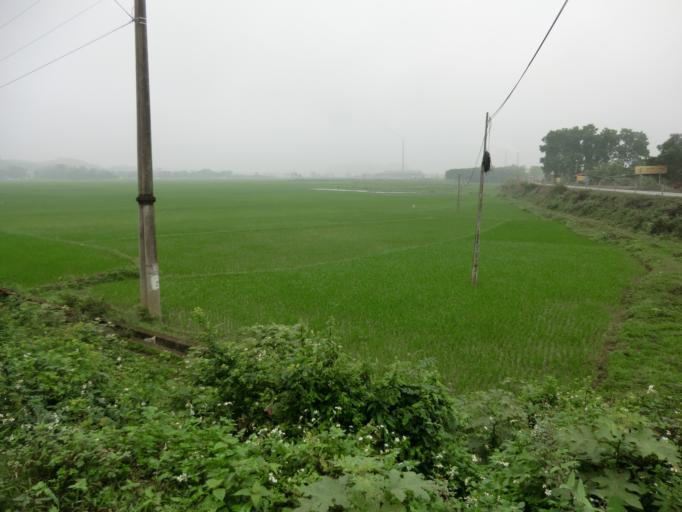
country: VN
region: Ha Noi
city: Dai Nghia
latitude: 20.6404
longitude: 105.6739
